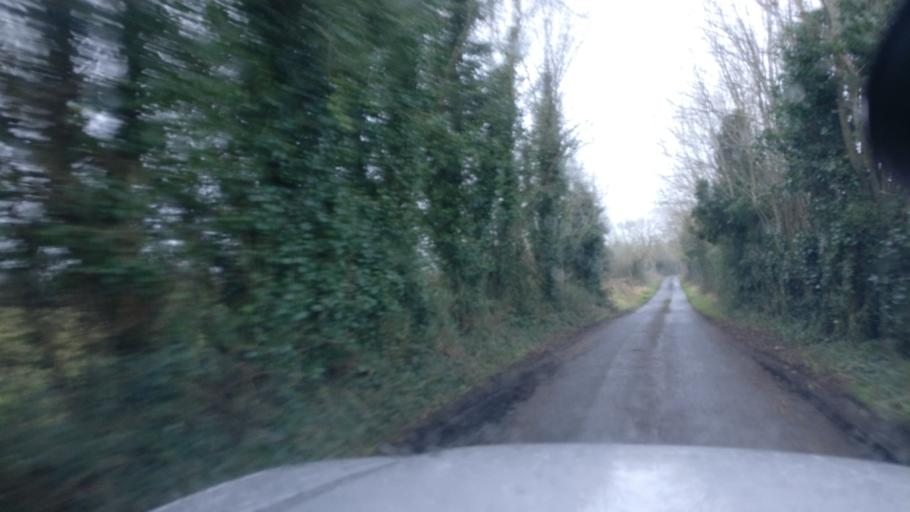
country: IE
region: Connaught
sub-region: County Galway
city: Loughrea
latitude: 53.2250
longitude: -8.5896
